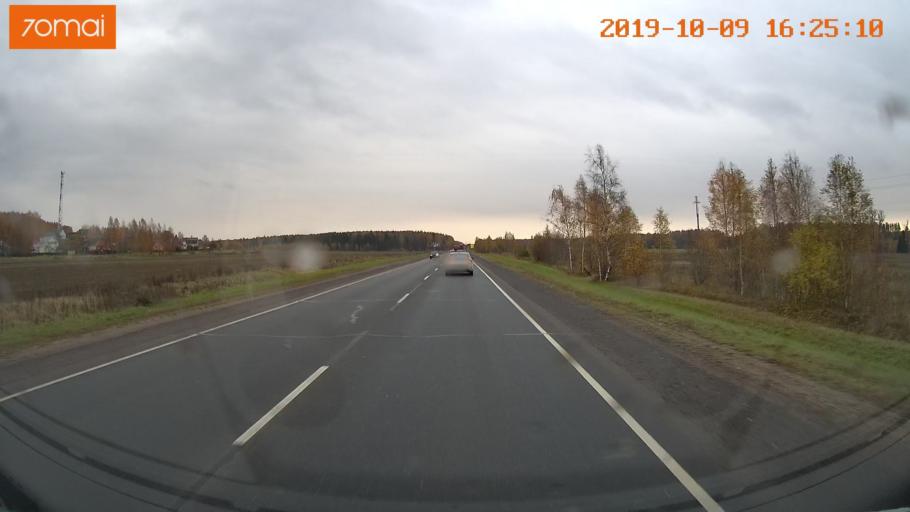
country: RU
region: Kostroma
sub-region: Kostromskoy Rayon
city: Kostroma
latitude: 57.6447
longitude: 40.9175
